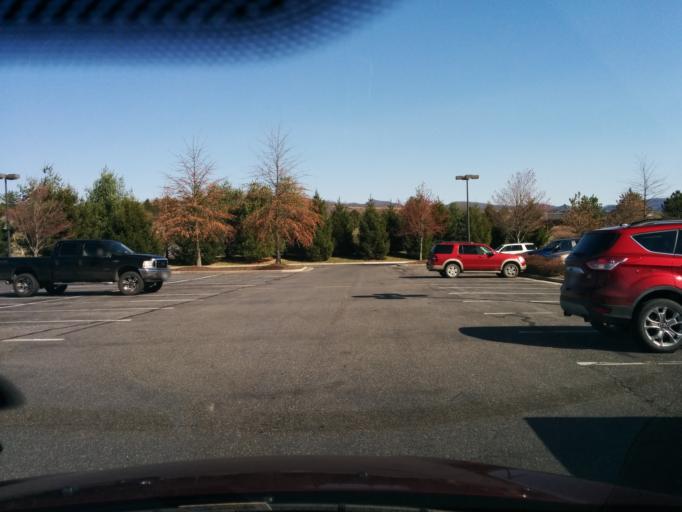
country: US
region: Virginia
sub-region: Rockbridge County
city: East Lexington
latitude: 37.8076
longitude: -79.4072
